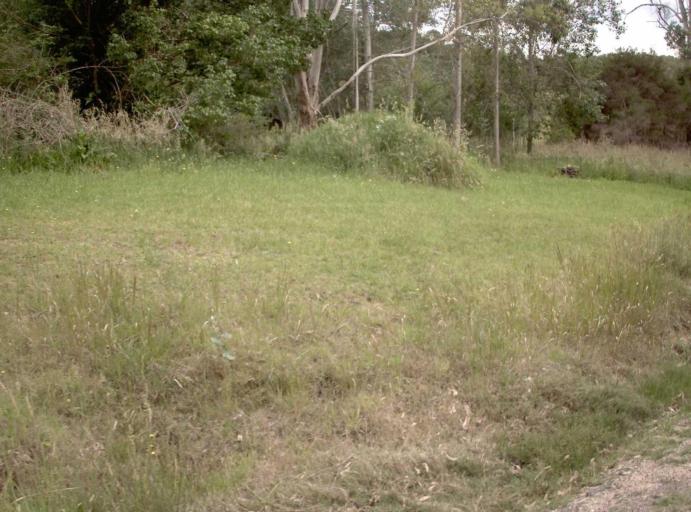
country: AU
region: New South Wales
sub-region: Bombala
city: Bombala
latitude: -37.4298
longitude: 149.1982
